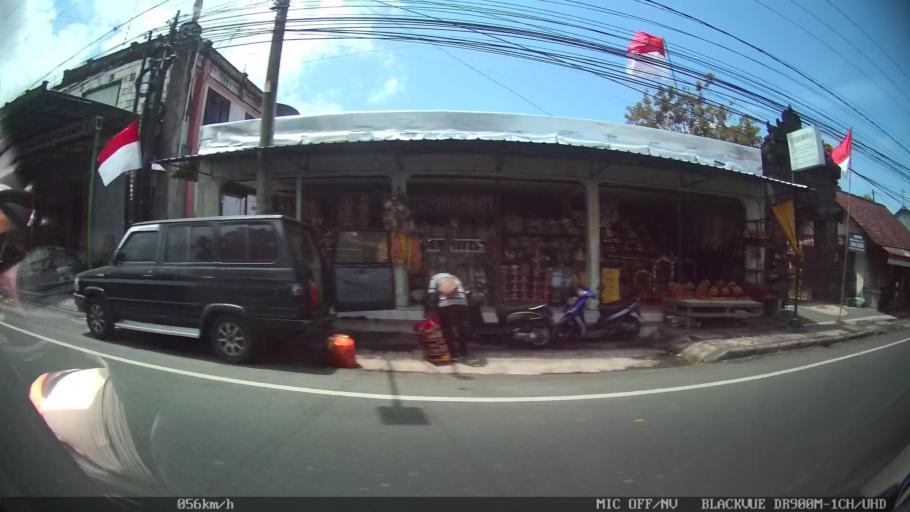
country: ID
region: Bali
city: Banjar Desa
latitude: -8.5887
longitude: 115.2825
